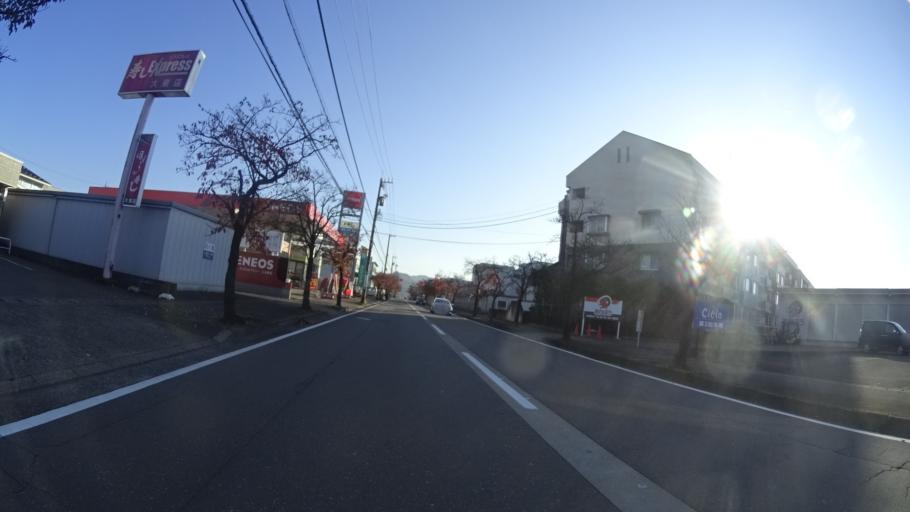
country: JP
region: Fukui
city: Fukui-shi
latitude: 36.0639
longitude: 136.2511
